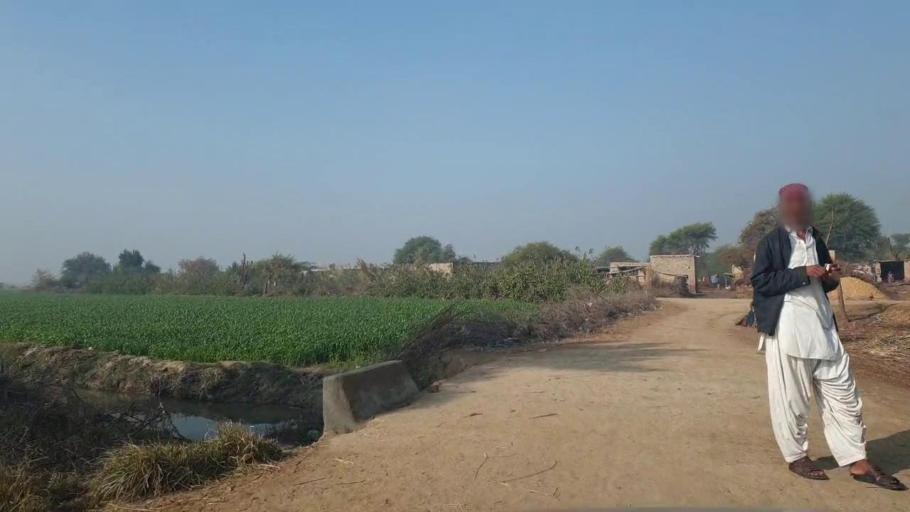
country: PK
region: Sindh
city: Shahdadpur
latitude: 25.9416
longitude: 68.5751
